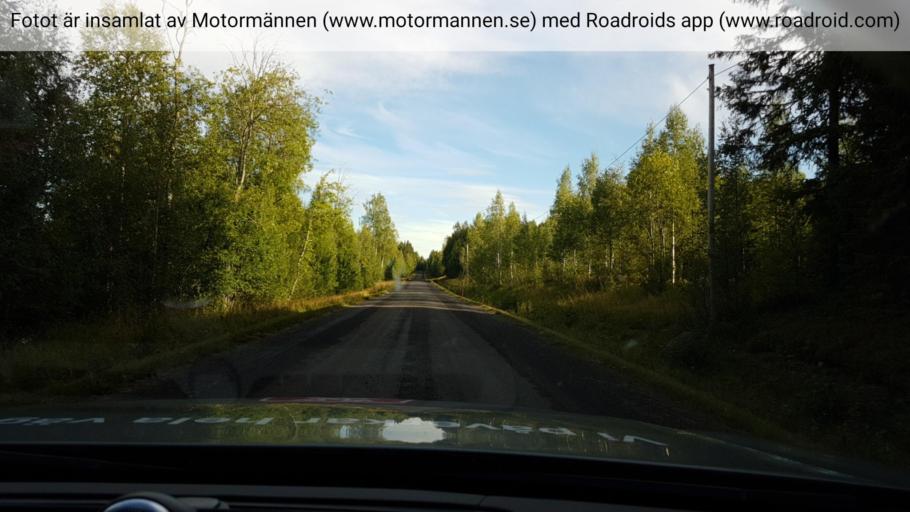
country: SE
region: Jaemtland
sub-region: Stroemsunds Kommun
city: Stroemsund
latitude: 64.1087
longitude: 15.8166
